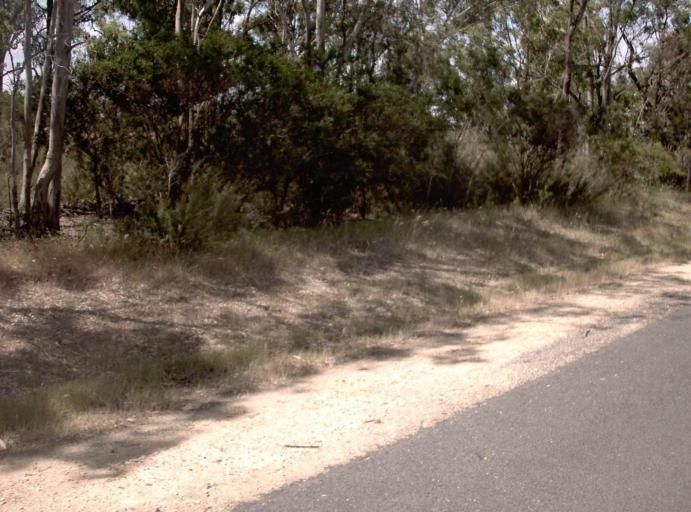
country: AU
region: Victoria
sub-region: Wellington
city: Sale
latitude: -37.9433
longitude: 147.1316
